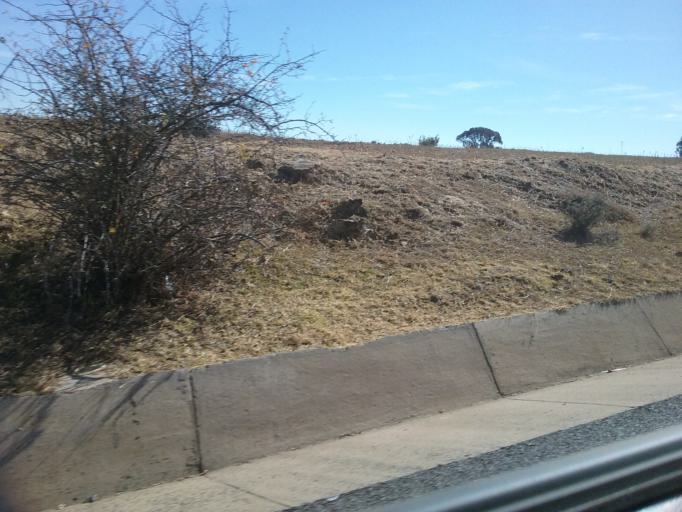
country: LS
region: Maseru
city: Maseru
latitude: -29.5002
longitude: 27.5710
